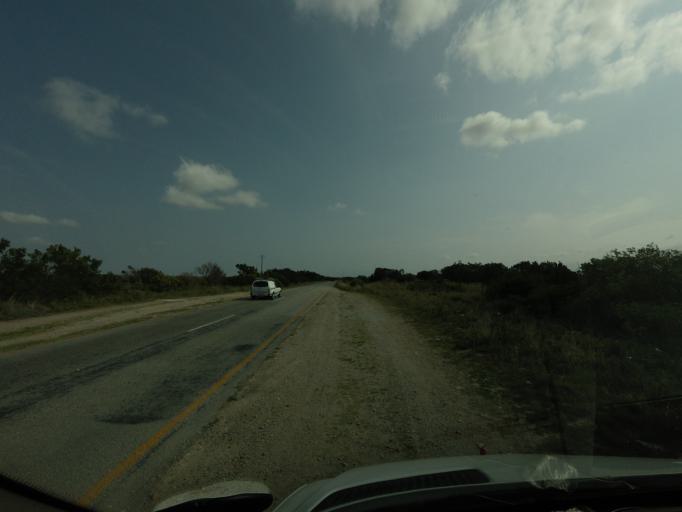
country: ZA
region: Eastern Cape
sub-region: Nelson Mandela Bay Metropolitan Municipality
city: Uitenhage
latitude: -33.6911
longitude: 25.5885
